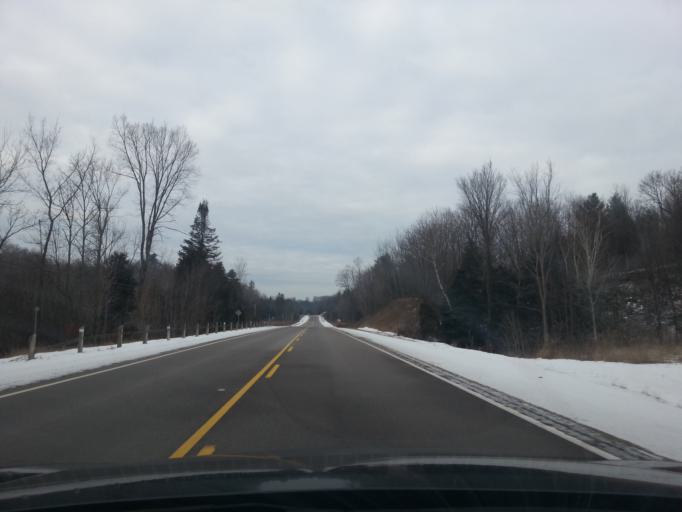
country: CA
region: Ontario
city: Skatepark
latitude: 44.7575
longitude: -76.7873
